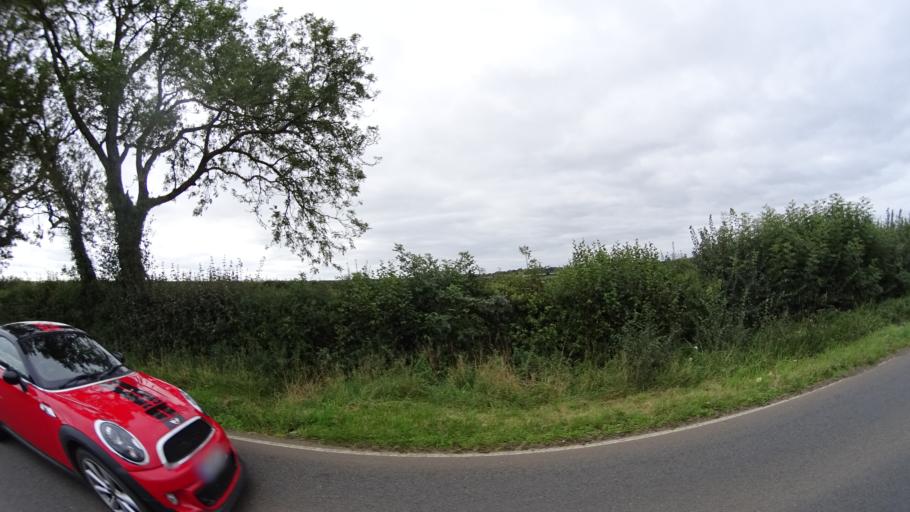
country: GB
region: England
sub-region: Dorset
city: Gillingham
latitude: 51.0516
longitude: -2.3285
